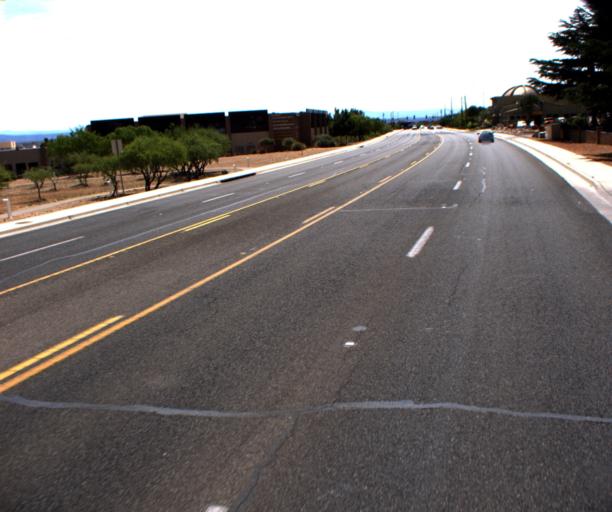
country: US
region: Arizona
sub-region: Yavapai County
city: Cottonwood
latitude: 34.7339
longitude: -112.0310
